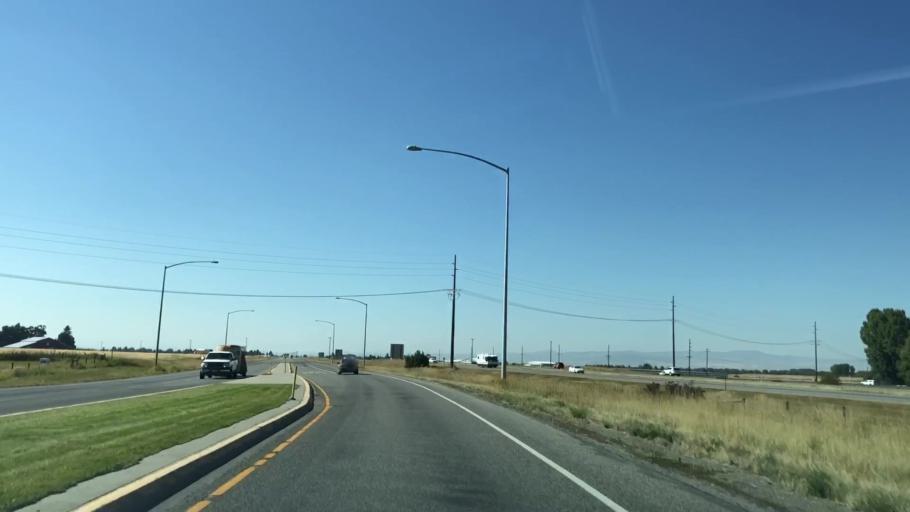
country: US
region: Montana
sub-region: Gallatin County
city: Bozeman
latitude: 45.7190
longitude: -111.0709
